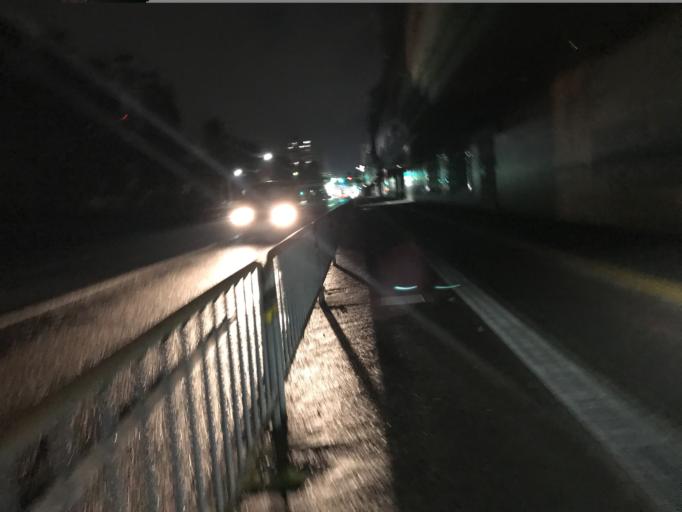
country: JP
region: Shiga Prefecture
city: Otsu-shi
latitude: 35.0177
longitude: 135.8609
